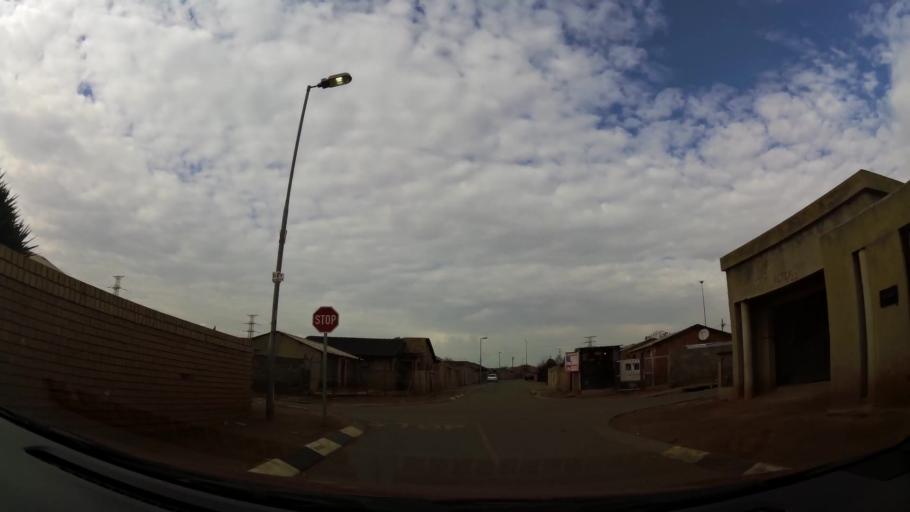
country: ZA
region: Gauteng
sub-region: City of Johannesburg Metropolitan Municipality
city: Soweto
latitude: -26.2423
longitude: 27.8535
